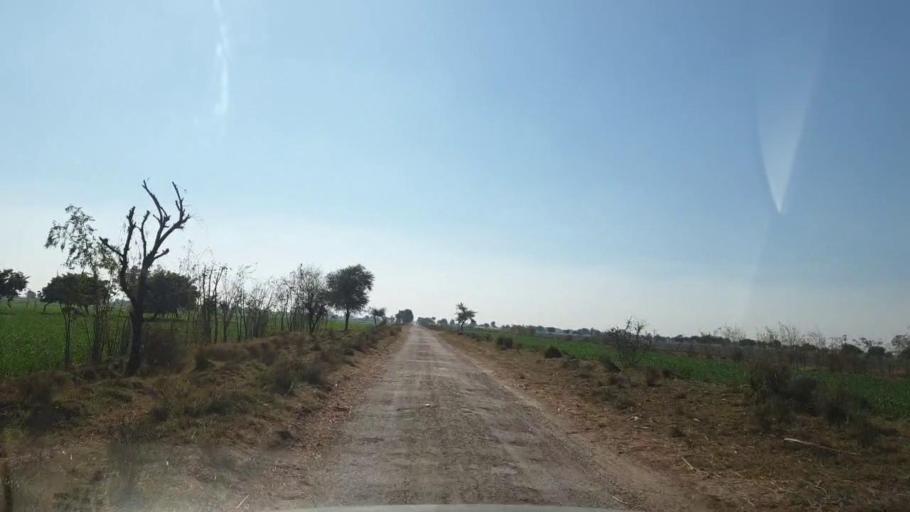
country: PK
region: Sindh
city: Jhol
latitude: 25.8216
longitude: 69.0359
